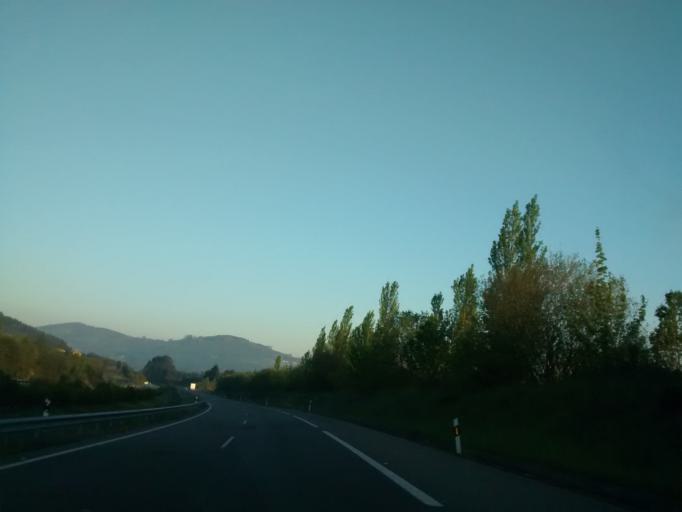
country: ES
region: Asturias
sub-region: Province of Asturias
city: Villaviciosa
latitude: 43.4997
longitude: -5.3845
